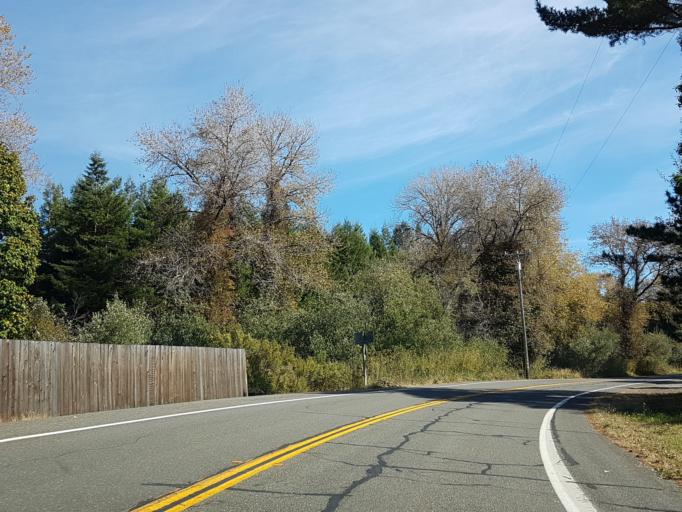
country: US
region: California
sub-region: Humboldt County
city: Rio Dell
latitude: 40.4460
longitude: -123.9891
